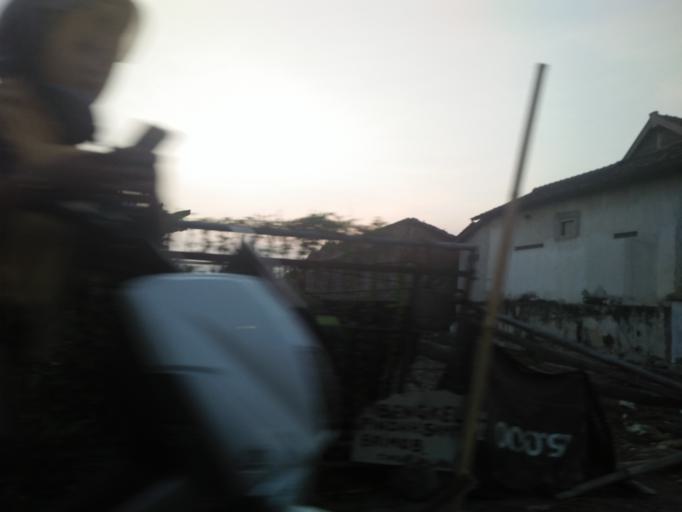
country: ID
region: Daerah Istimewa Yogyakarta
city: Sewon
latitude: -7.8388
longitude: 110.3916
